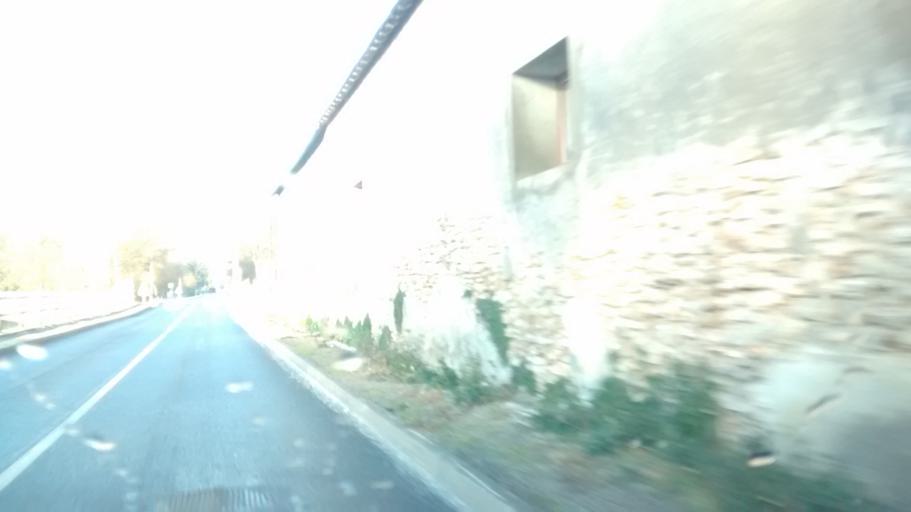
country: FR
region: Centre
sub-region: Departement d'Indre-et-Loire
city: Esvres
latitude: 47.2805
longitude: 0.7954
